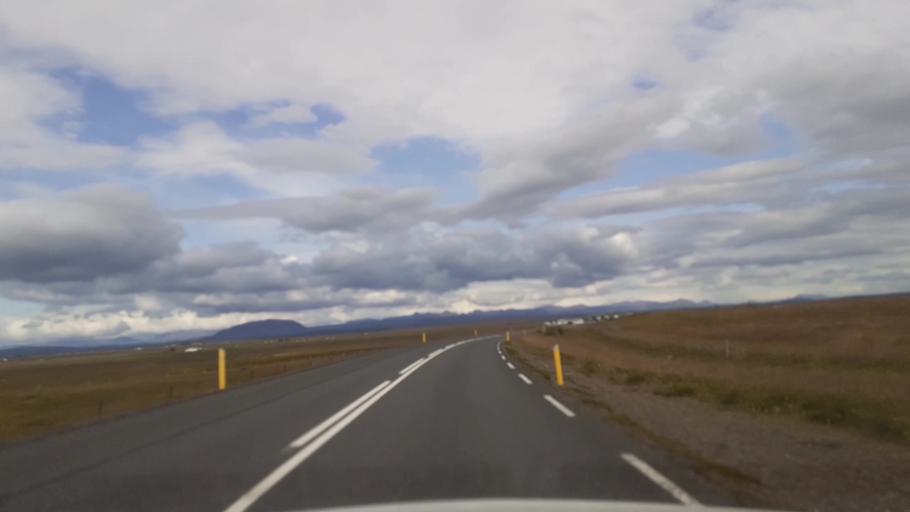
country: IS
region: South
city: Selfoss
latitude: 63.9240
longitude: -20.8521
